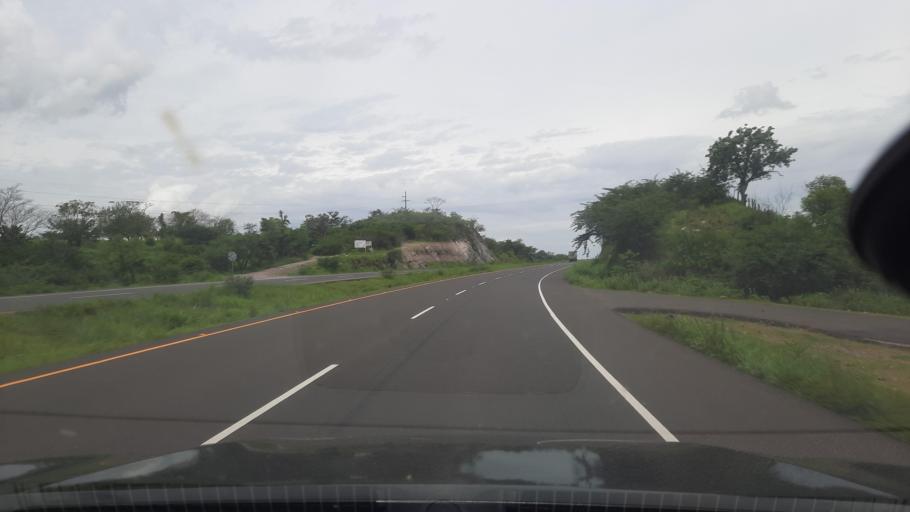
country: HN
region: Valle
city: Aramecina
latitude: 13.7758
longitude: -87.6996
